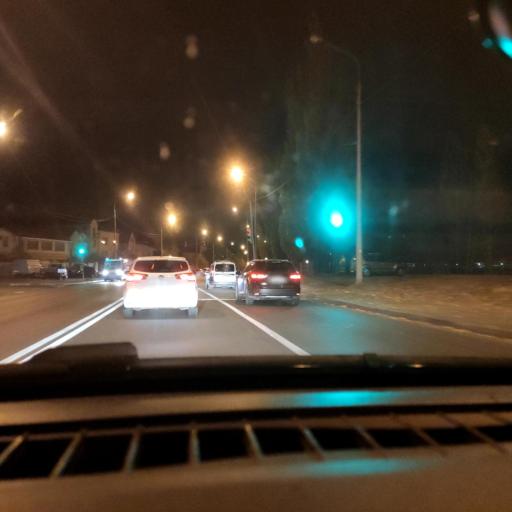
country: RU
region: Voronezj
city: Voronezh
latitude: 51.6782
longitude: 39.2272
